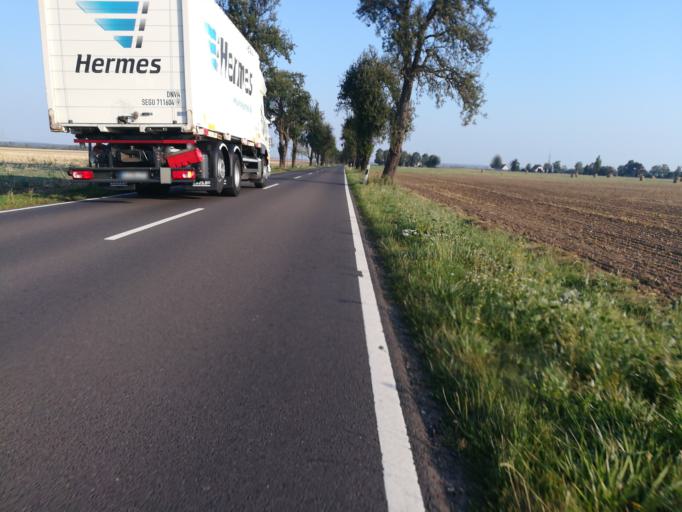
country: DE
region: Saxony-Anhalt
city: Gross Santersleben
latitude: 52.2334
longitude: 11.4448
